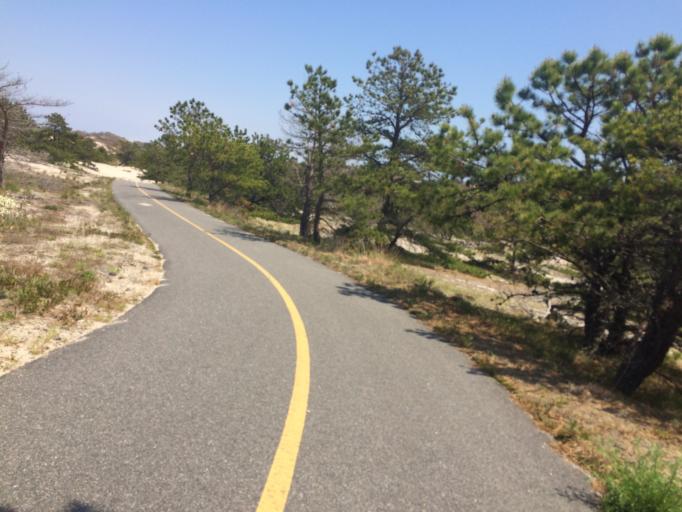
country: US
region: Massachusetts
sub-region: Barnstable County
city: Provincetown
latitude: 42.0666
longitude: -70.2138
